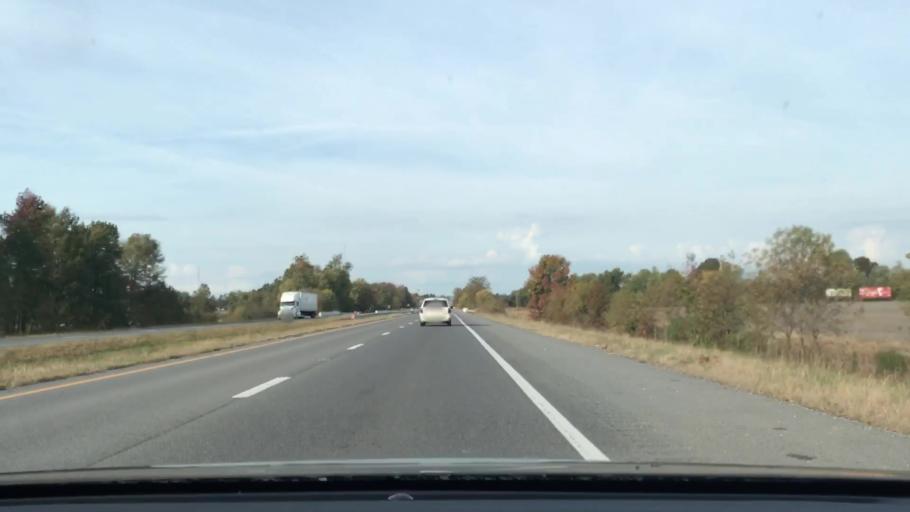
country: US
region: Kentucky
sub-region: Graves County
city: Mayfield
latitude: 36.7695
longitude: -88.6252
